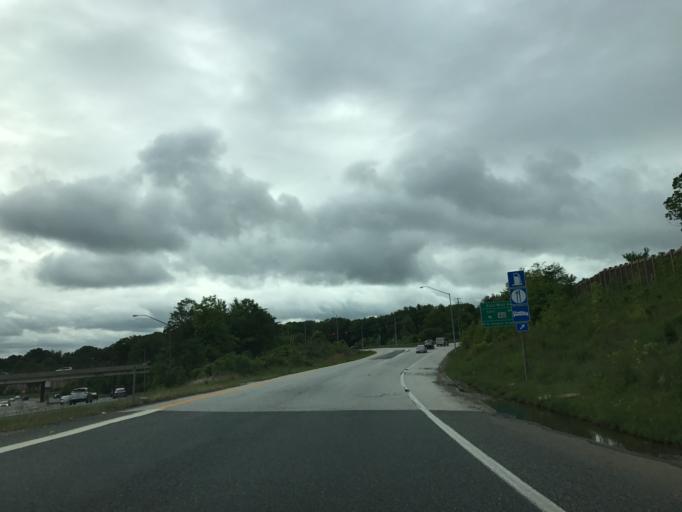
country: US
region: Maryland
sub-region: Prince George's County
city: Landover Hills
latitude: 38.9440
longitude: -76.8786
